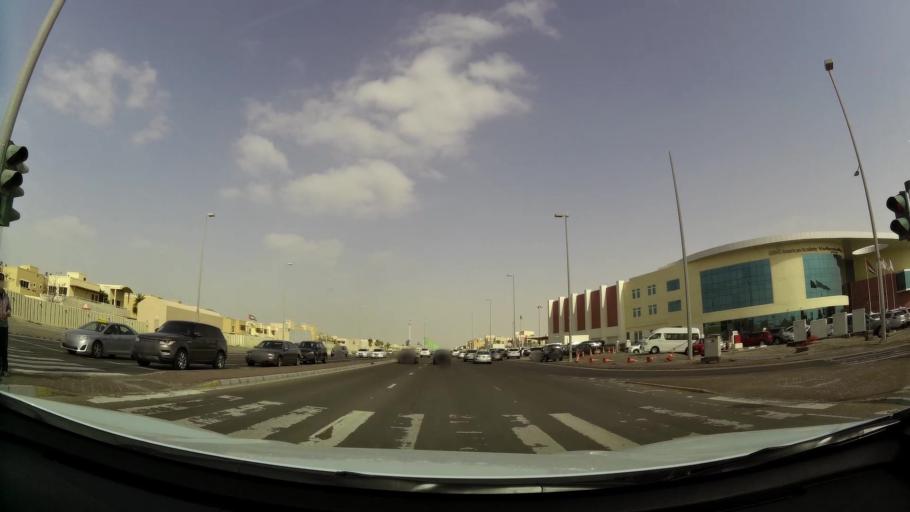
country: AE
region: Abu Dhabi
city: Abu Dhabi
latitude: 24.4297
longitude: 54.5636
